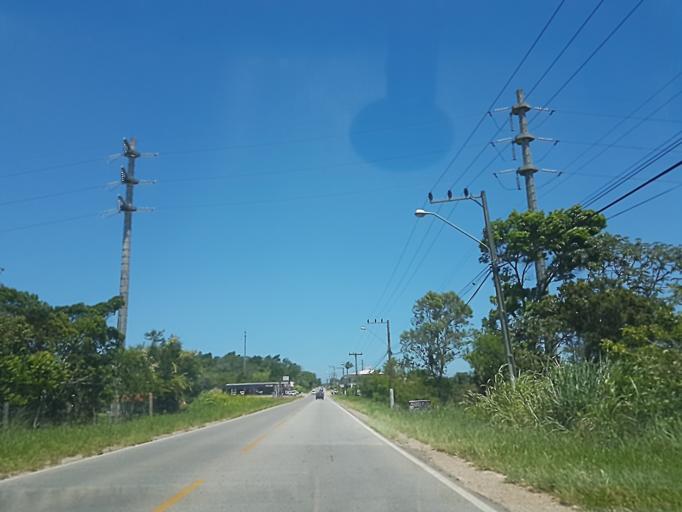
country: BR
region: Santa Catarina
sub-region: Jaguaruna
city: Jaguaruna
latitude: -28.6076
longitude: -49.0312
